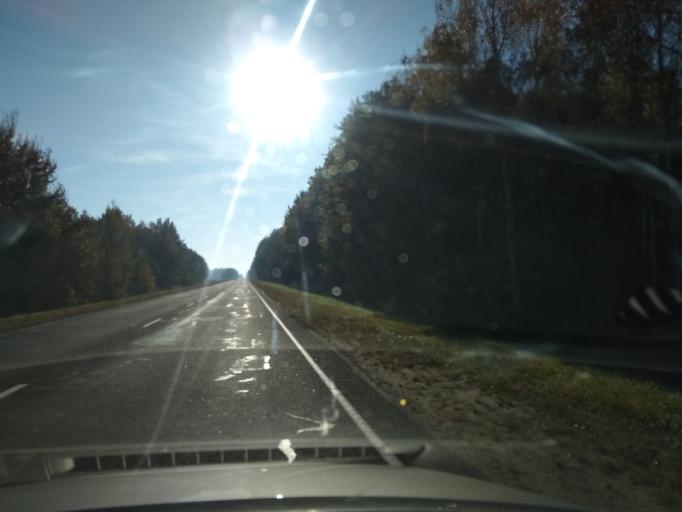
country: BY
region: Brest
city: Malaryta
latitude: 51.8827
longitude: 24.1588
